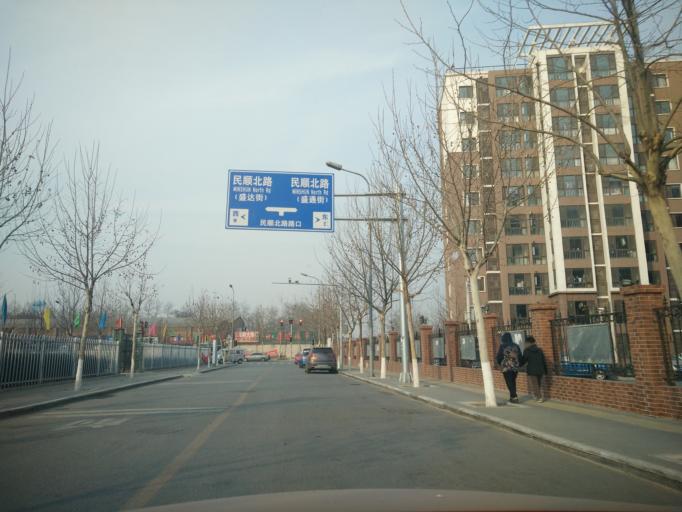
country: CN
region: Beijing
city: Yinghai
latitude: 39.7165
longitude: 116.3961
